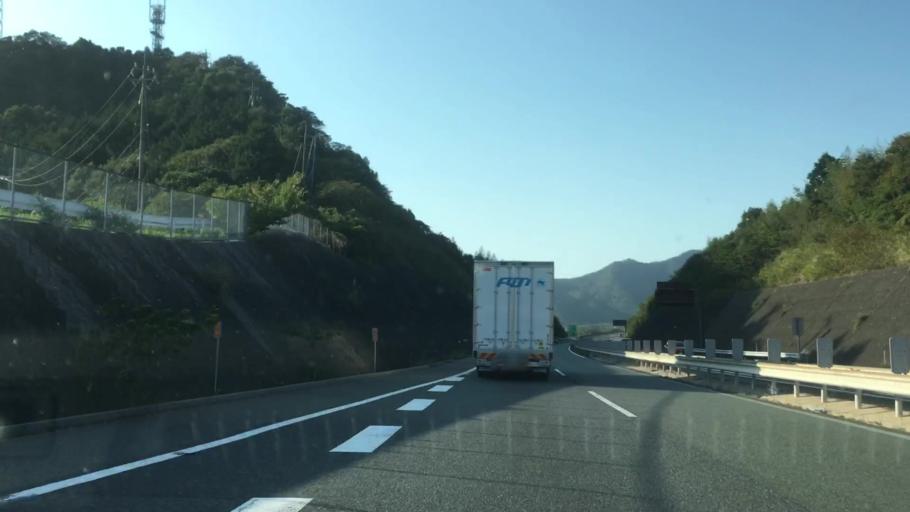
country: JP
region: Yamaguchi
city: Ogori-shimogo
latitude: 34.0894
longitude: 131.4604
